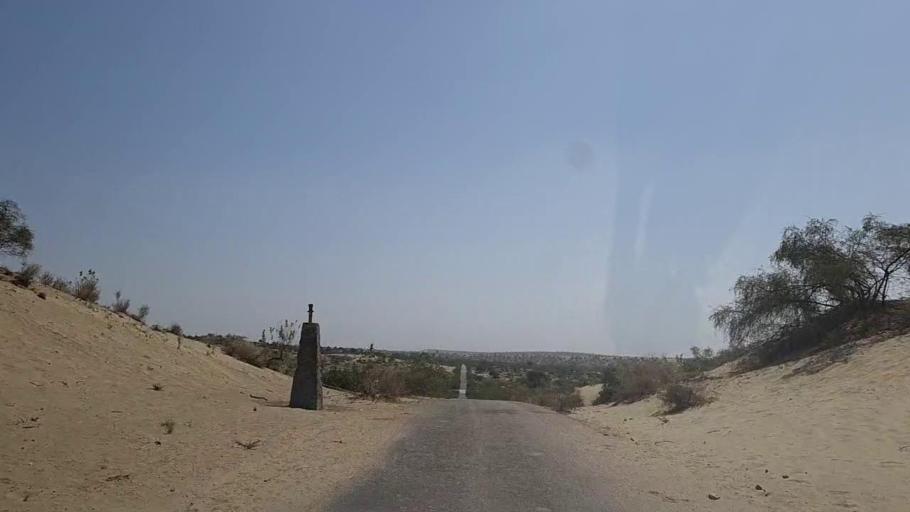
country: PK
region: Sindh
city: Diplo
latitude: 24.4998
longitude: 69.4291
